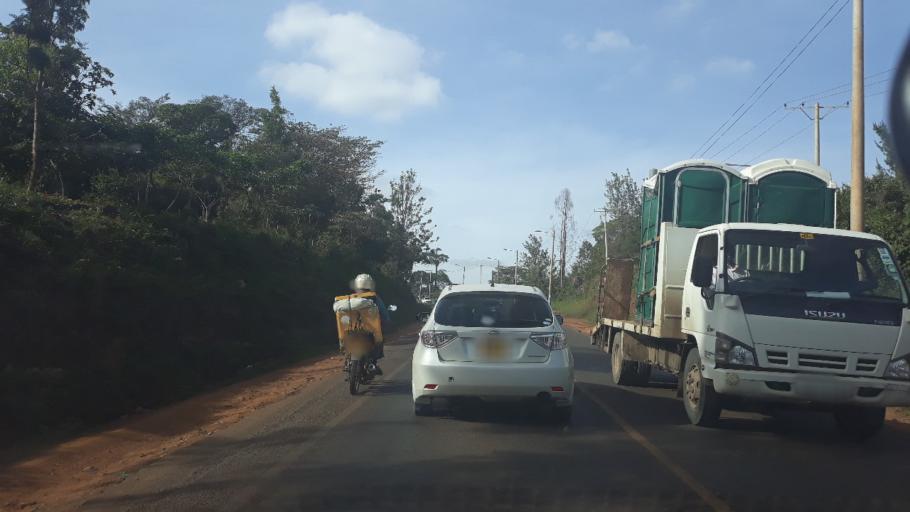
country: KE
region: Nairobi Area
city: Pumwani
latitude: -1.2339
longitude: 36.8434
